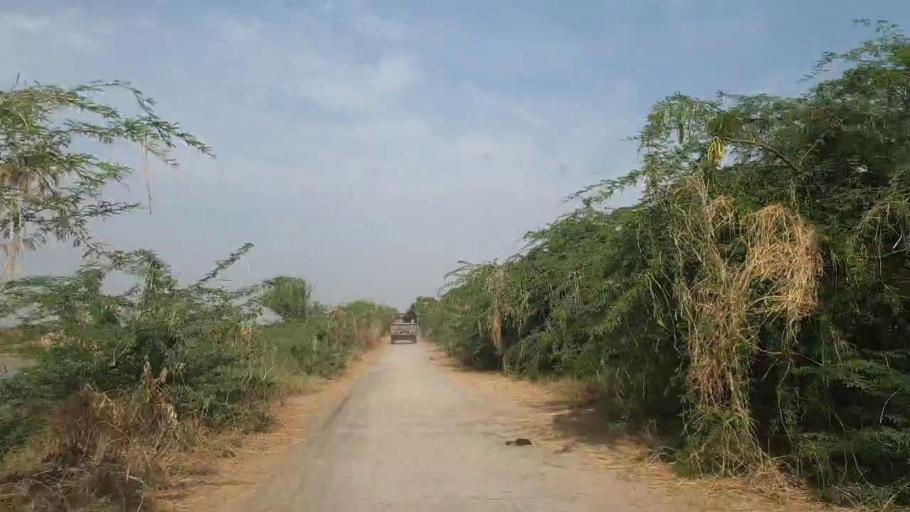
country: PK
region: Sindh
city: Tando Bago
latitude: 24.9143
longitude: 68.9957
